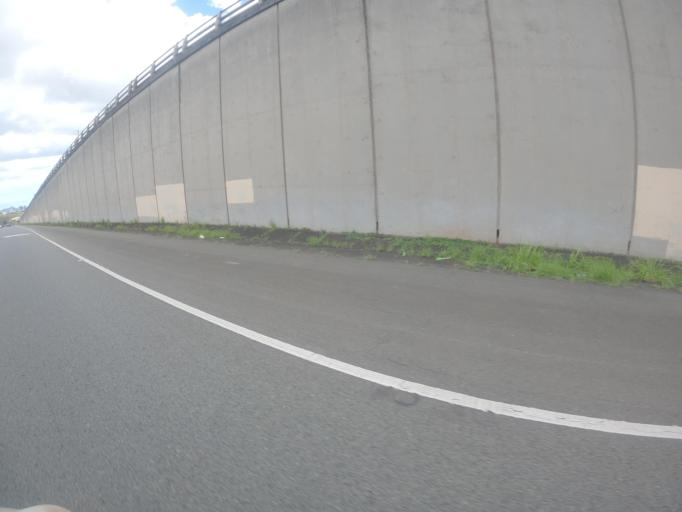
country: US
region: Hawaii
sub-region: Honolulu County
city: Halawa Heights
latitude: 21.3659
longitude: -157.9039
